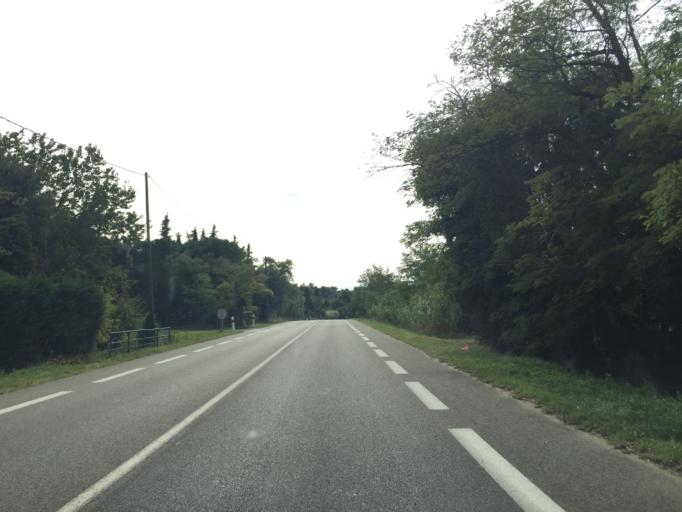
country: FR
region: Provence-Alpes-Cote d'Azur
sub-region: Departement du Vaucluse
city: Bollene
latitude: 44.2600
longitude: 4.7405
